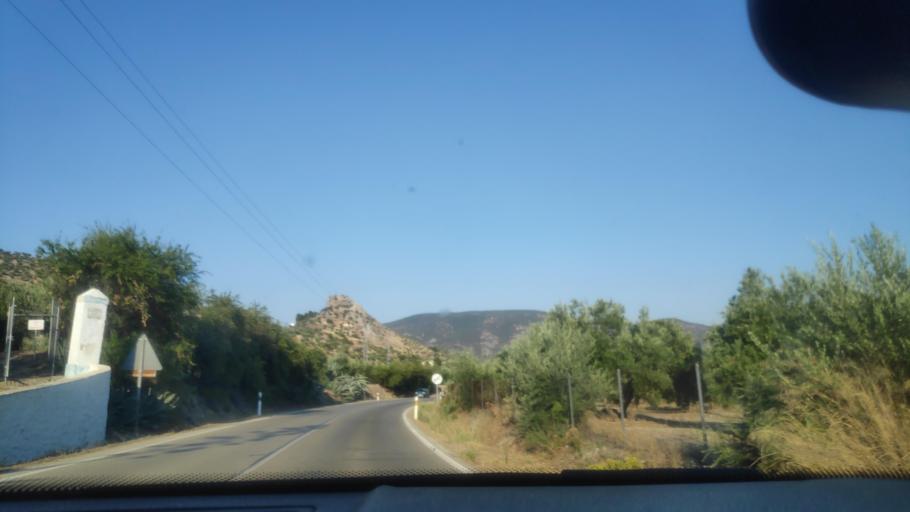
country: ES
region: Andalusia
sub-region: Provincia de Jaen
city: Jaen
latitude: 37.7476
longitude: -3.7848
